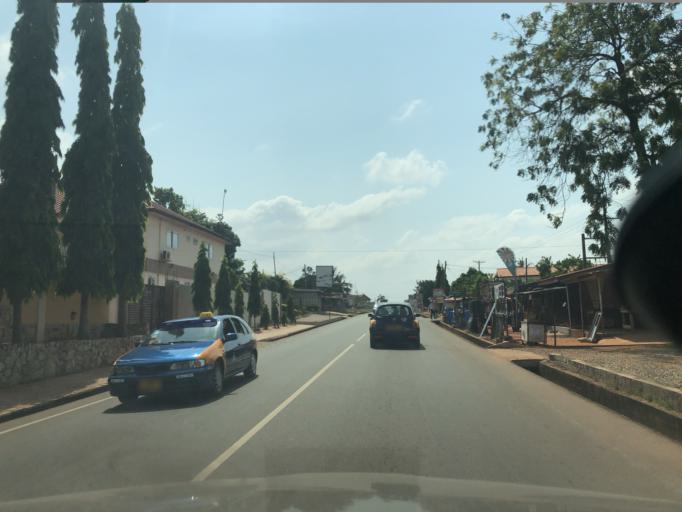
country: GH
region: Greater Accra
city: Medina Estates
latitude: 5.6730
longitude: -0.1904
